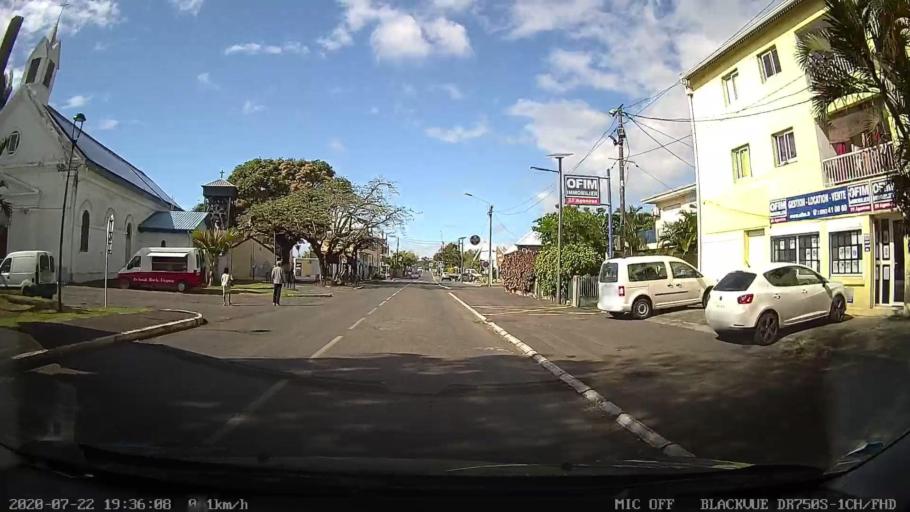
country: RE
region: Reunion
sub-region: Reunion
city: Sainte-Suzanne
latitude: -20.9061
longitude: 55.6074
